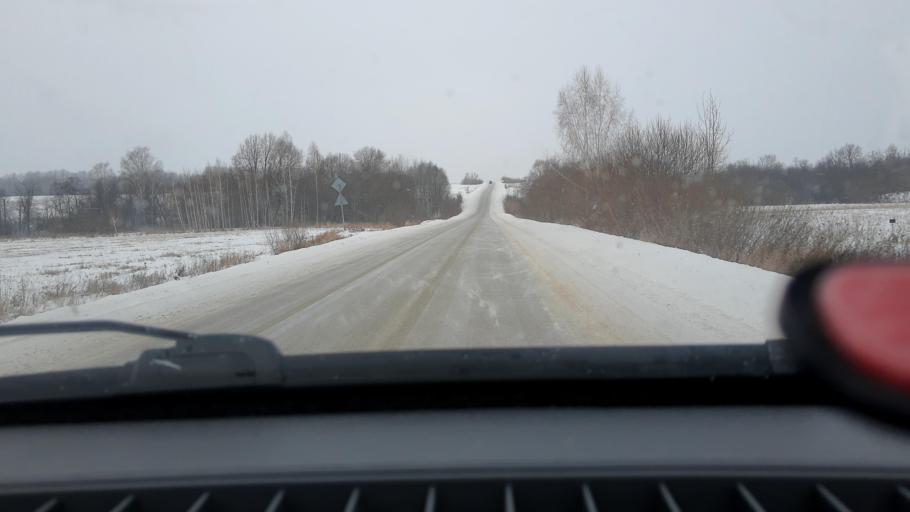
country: RU
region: Bashkortostan
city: Iglino
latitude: 54.6994
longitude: 56.4161
